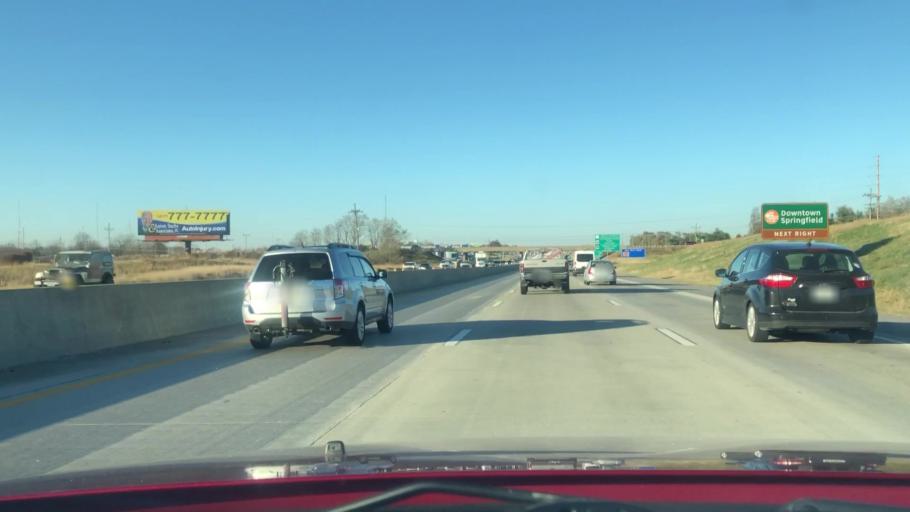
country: US
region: Missouri
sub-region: Greene County
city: Springfield
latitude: 37.1998
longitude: -93.2261
